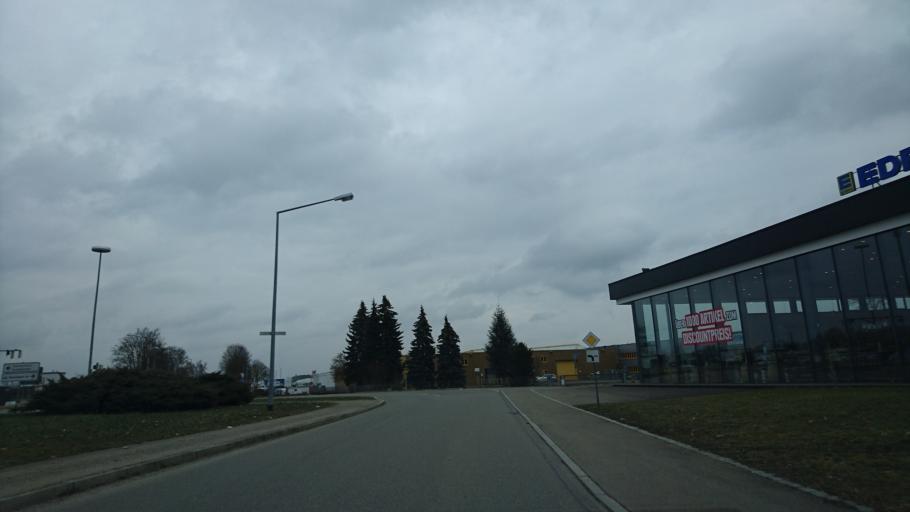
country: DE
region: Bavaria
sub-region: Swabia
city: Dillingen an der Donau
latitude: 48.5873
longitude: 10.5145
